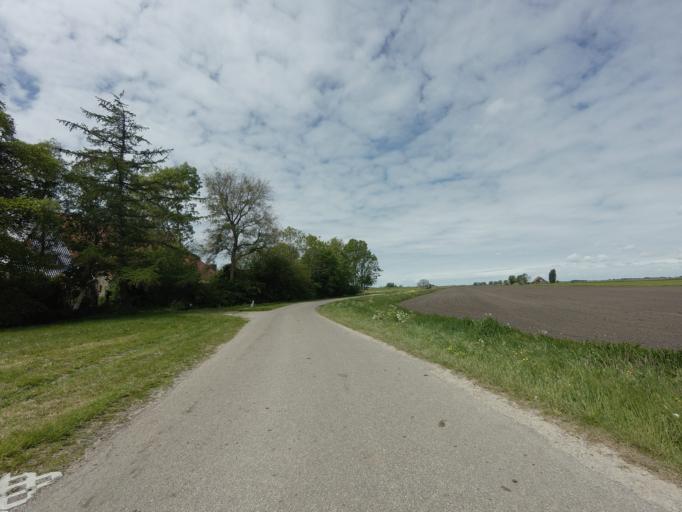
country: NL
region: Friesland
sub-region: Gemeente Gaasterlan-Sleat
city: Oudemirdum
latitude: 52.8984
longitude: 5.5115
